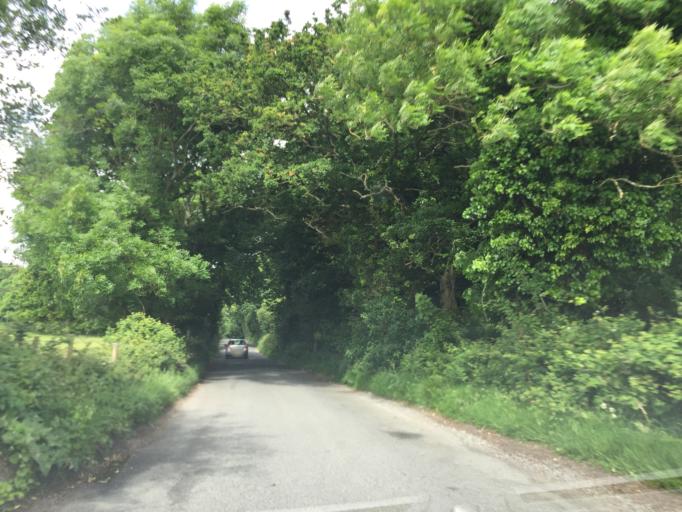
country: GB
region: England
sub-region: Dorset
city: Dorchester
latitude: 50.7201
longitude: -2.3776
